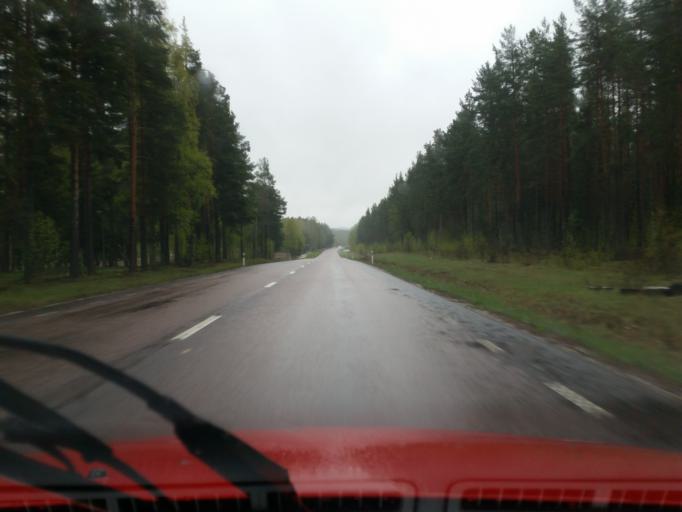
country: SE
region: Dalarna
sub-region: Borlange Kommun
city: Borlaenge
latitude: 60.5224
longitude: 15.3589
